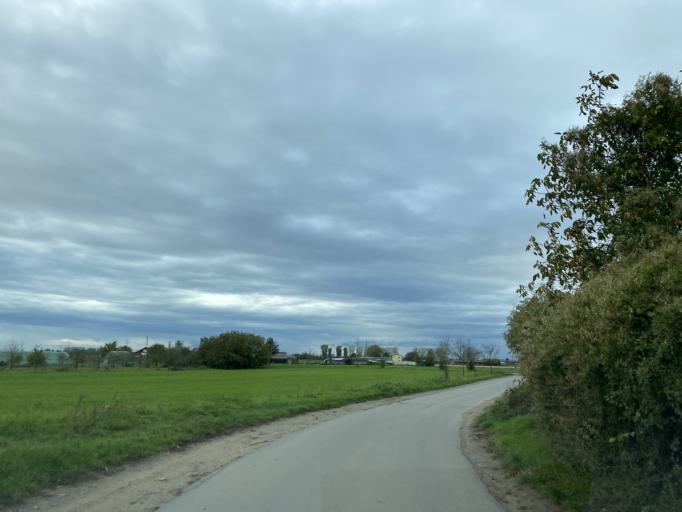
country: DE
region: Hesse
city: Pfungstadt
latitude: 49.7865
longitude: 8.5993
